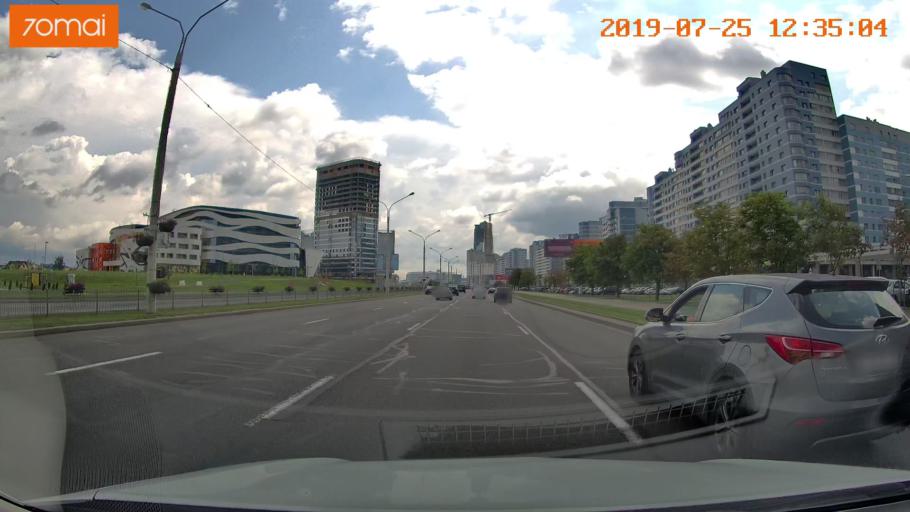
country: BY
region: Minsk
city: Zhdanovichy
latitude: 53.9424
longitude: 27.4651
